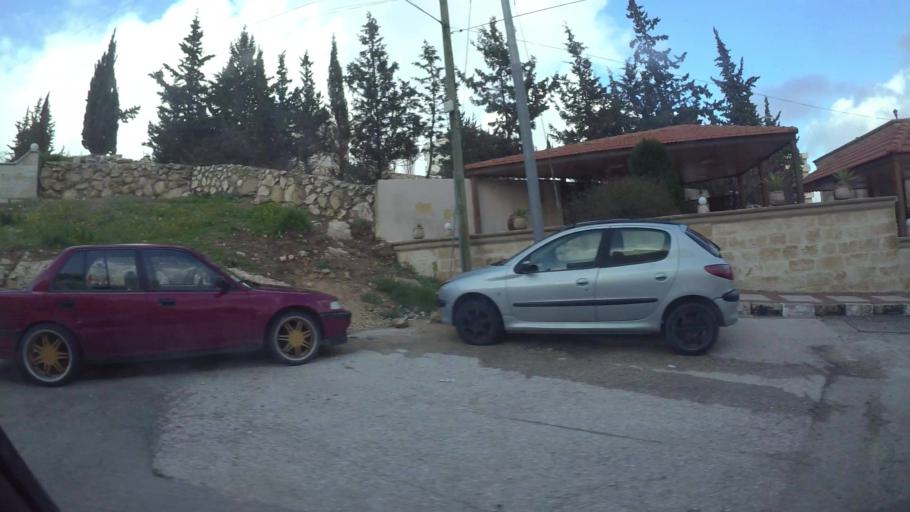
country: JO
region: Amman
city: Al Jubayhah
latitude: 32.0535
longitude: 35.8917
